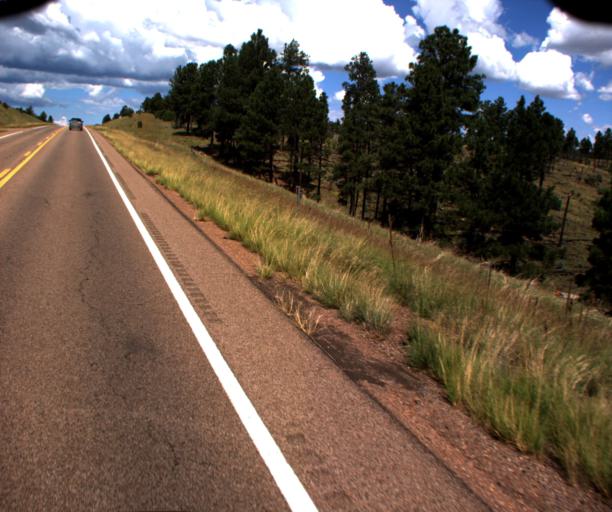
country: US
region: Arizona
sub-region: Navajo County
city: Heber-Overgaard
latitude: 34.3730
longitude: -110.4592
